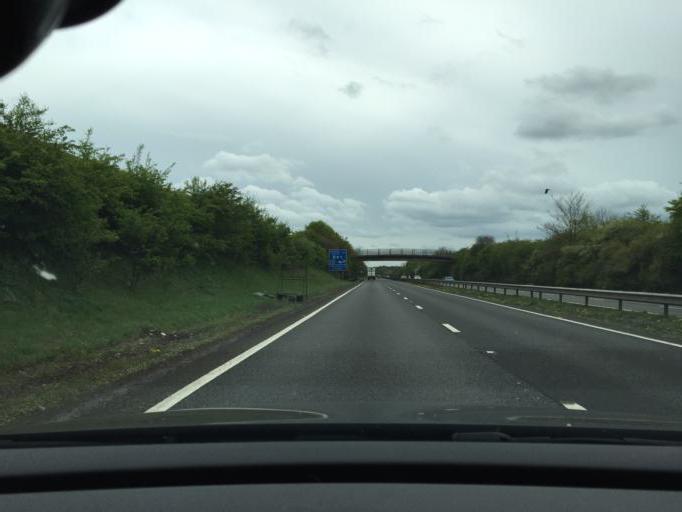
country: GB
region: England
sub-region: West Berkshire
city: Hermitage
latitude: 51.4699
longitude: -1.3049
